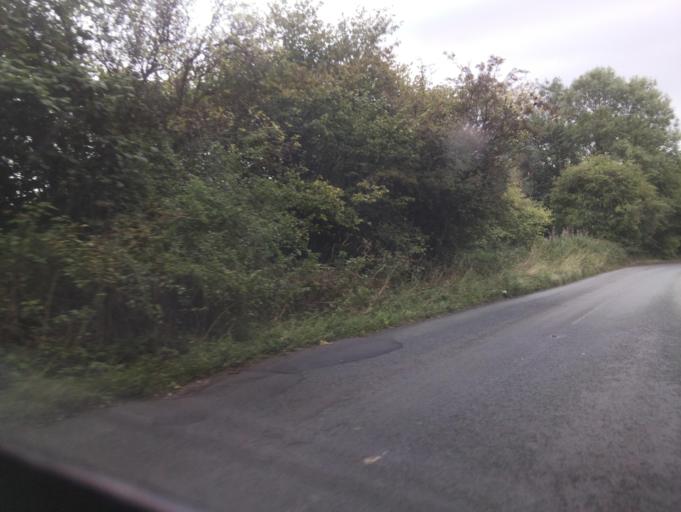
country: GB
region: England
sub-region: Kirklees
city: Clayton West
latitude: 53.6153
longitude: -1.5952
